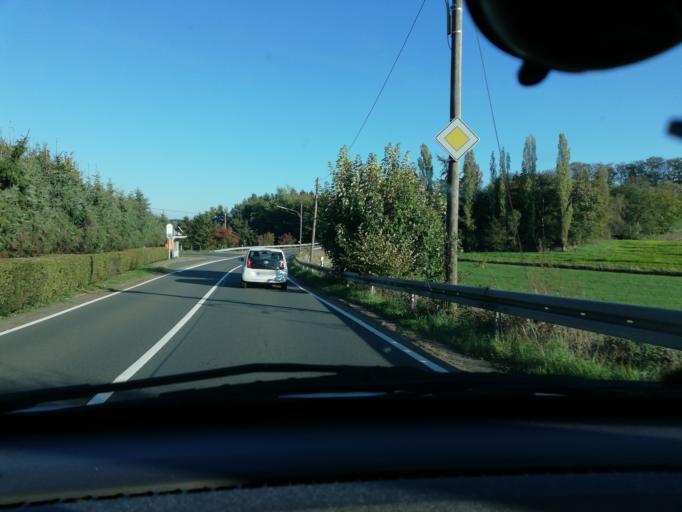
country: DE
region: North Rhine-Westphalia
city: Sprockhovel
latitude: 51.3830
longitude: 7.2417
